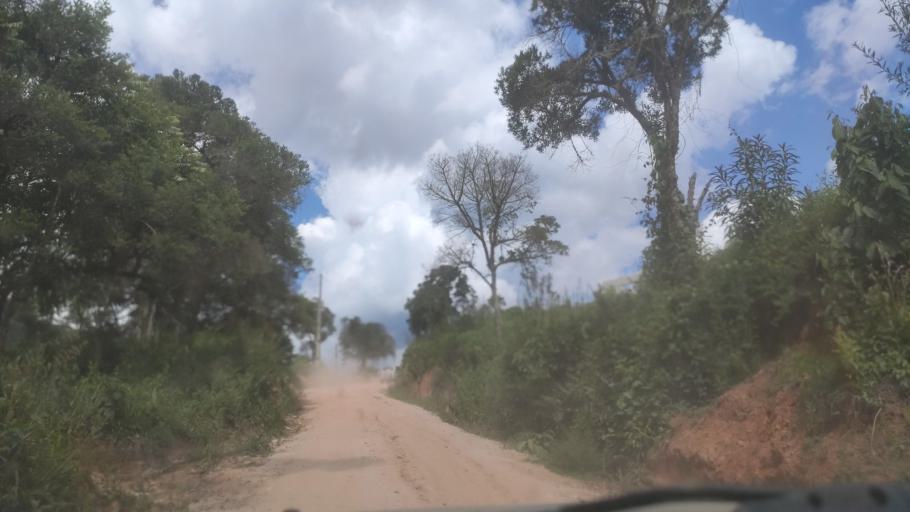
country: BR
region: Minas Gerais
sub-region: Camanducaia
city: Camanducaia
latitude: -22.7679
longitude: -45.9894
